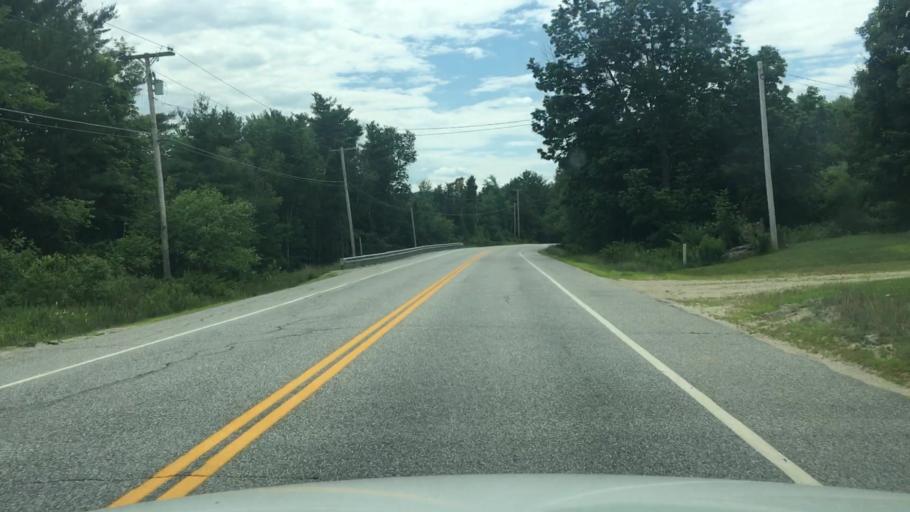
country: US
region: Maine
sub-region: Oxford County
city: West Paris
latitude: 44.3339
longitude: -70.5436
